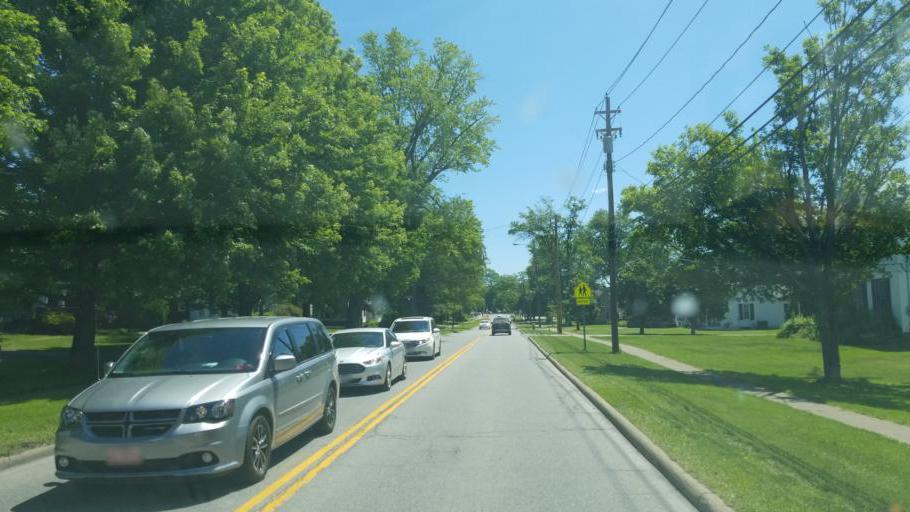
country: US
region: Ohio
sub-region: Geauga County
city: Burton
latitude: 41.4708
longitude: -81.1506
